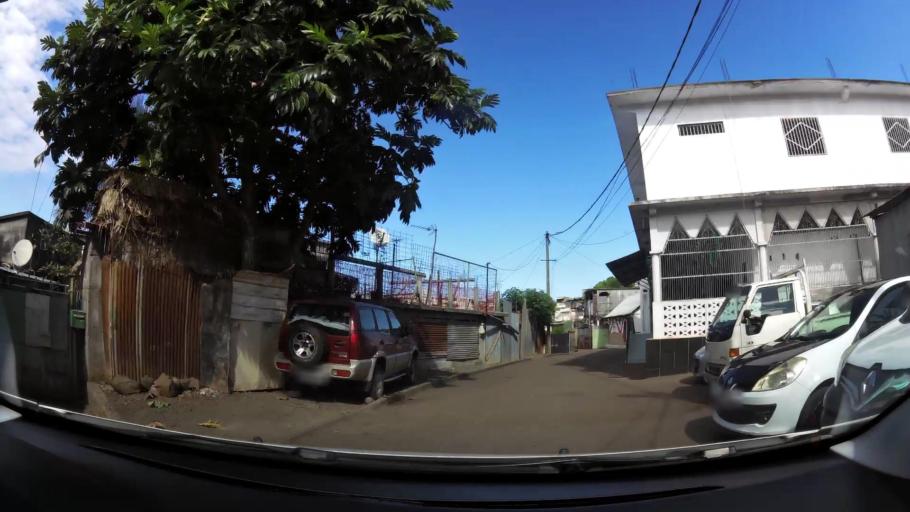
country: YT
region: Mamoudzou
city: Mamoudzou
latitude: -12.7844
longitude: 45.2190
